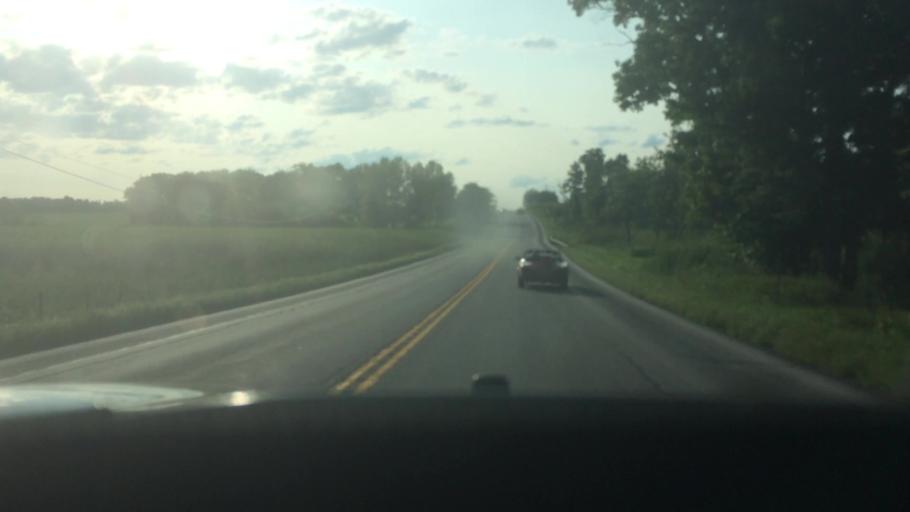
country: US
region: New York
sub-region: St. Lawrence County
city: Canton
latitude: 44.6521
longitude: -75.3035
